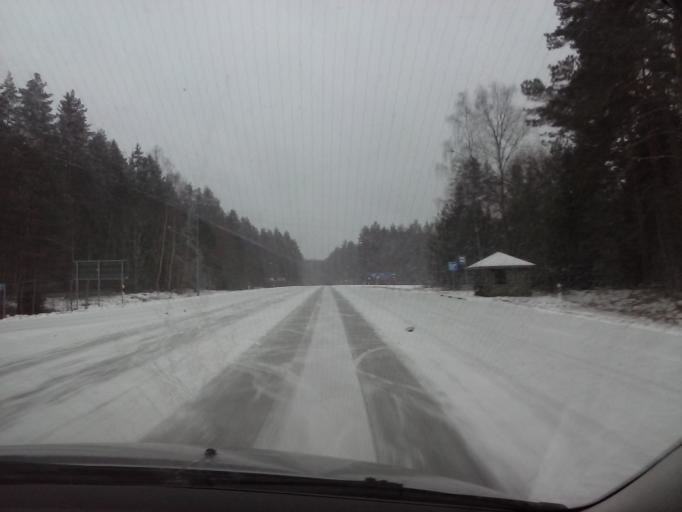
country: EE
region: Valgamaa
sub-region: Torva linn
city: Torva
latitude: 58.0114
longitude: 26.1630
